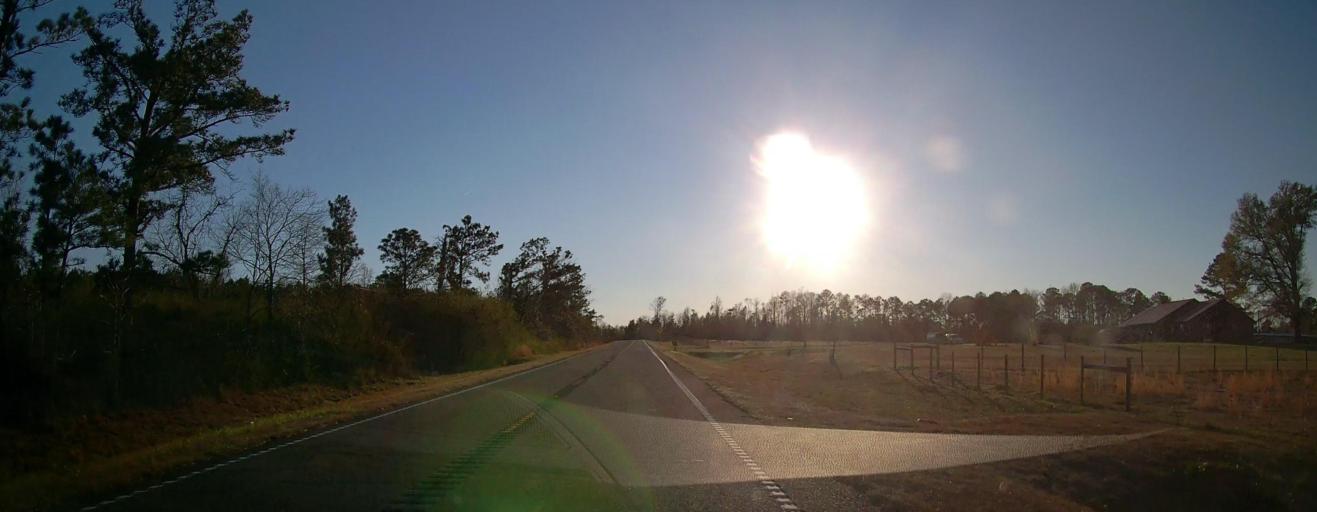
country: US
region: Georgia
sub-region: Talbot County
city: Talbotton
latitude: 32.6562
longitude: -84.6648
